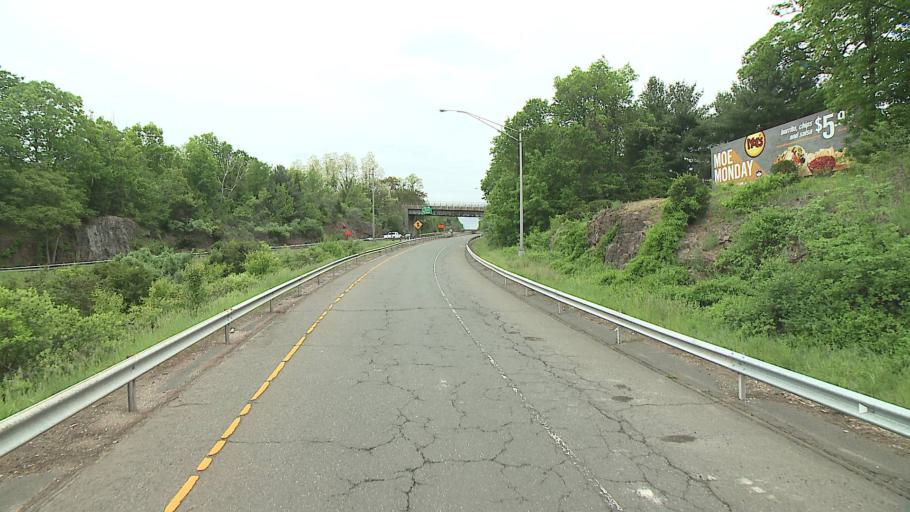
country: US
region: Connecticut
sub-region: Hartford County
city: Plainville
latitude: 41.6697
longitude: -72.8214
